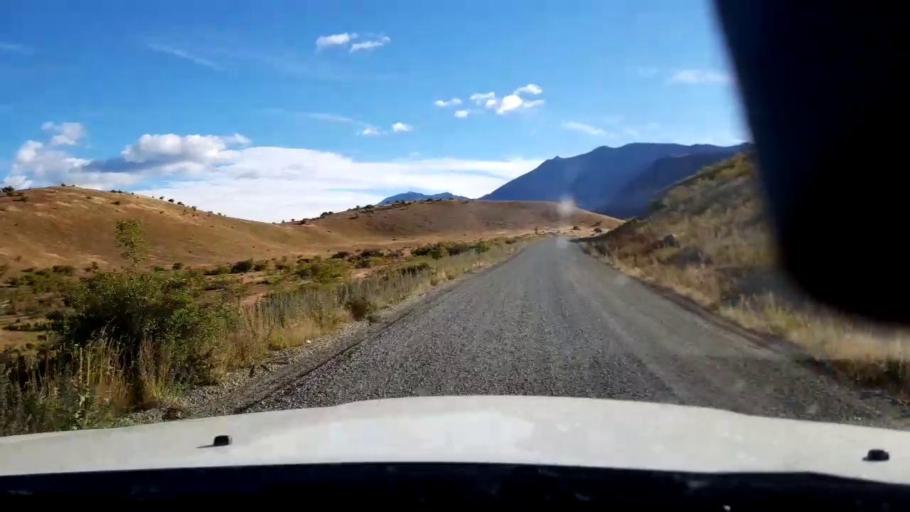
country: NZ
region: Canterbury
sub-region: Timaru District
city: Pleasant Point
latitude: -43.9670
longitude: 170.5176
